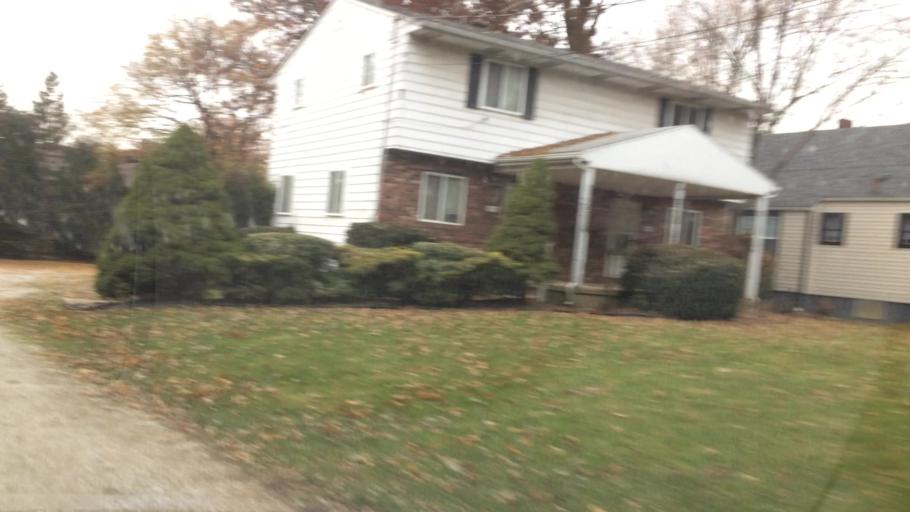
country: US
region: Ohio
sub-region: Summit County
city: Cuyahoga Falls
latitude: 41.1329
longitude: -81.4642
